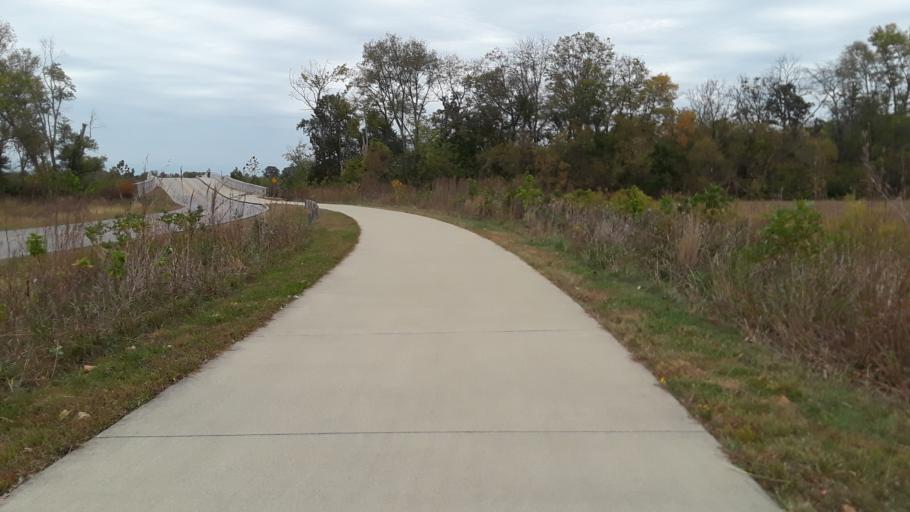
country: US
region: Kentucky
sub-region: Jefferson County
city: Middletown
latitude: 38.2061
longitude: -85.4745
